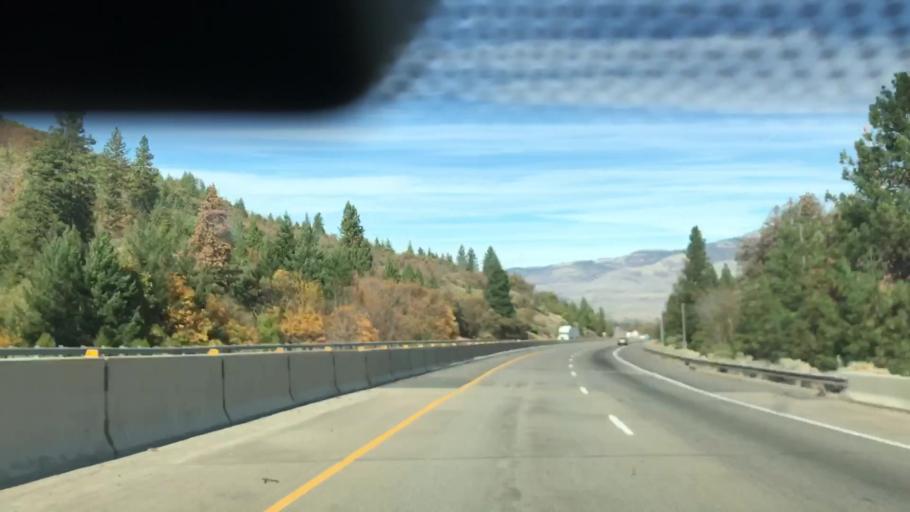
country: US
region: Oregon
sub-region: Jackson County
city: Ashland
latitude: 42.1353
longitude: -122.6353
